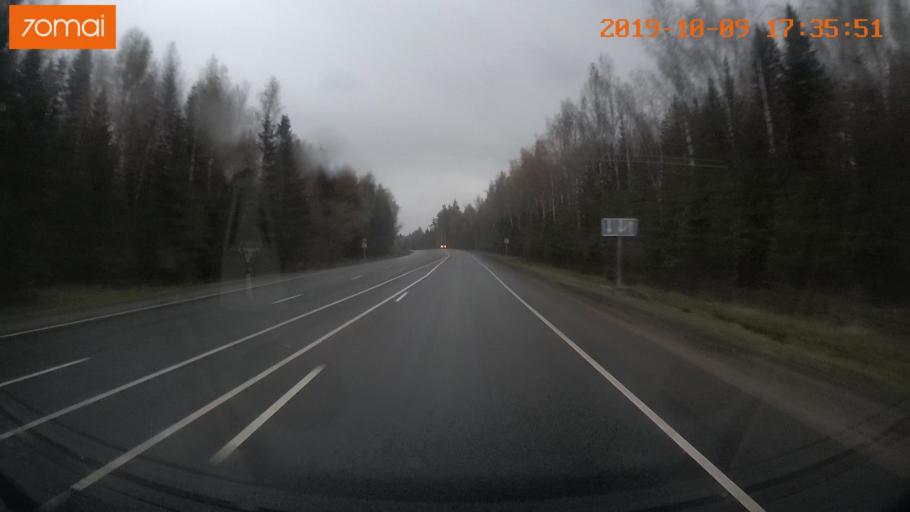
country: RU
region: Ivanovo
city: Bogorodskoye
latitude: 57.0873
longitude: 40.9993
